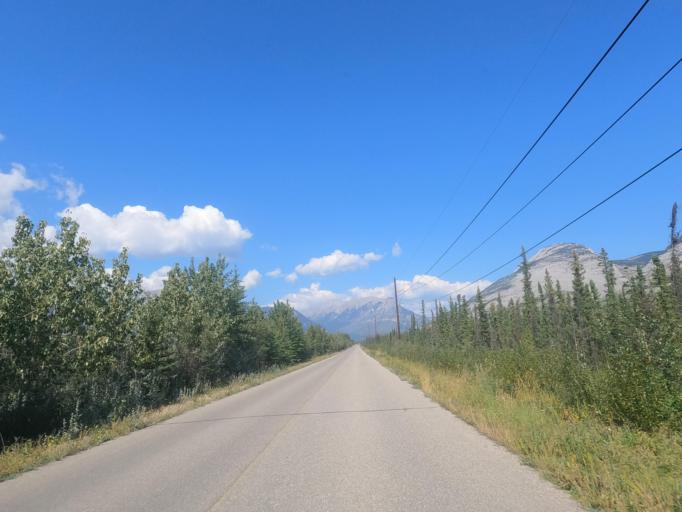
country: CA
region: Alberta
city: Jasper Park Lodge
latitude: 53.0021
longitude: -118.0851
